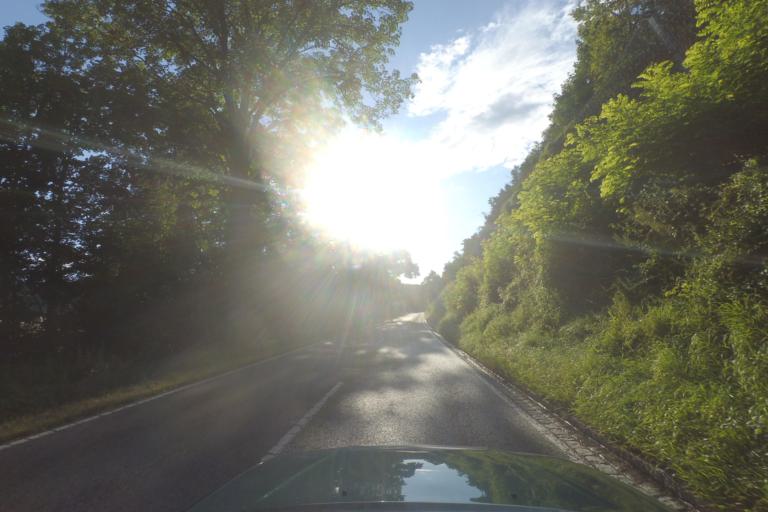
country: DE
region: Bavaria
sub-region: Upper Bavaria
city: Bohmfeld
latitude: 48.9365
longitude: 11.3691
